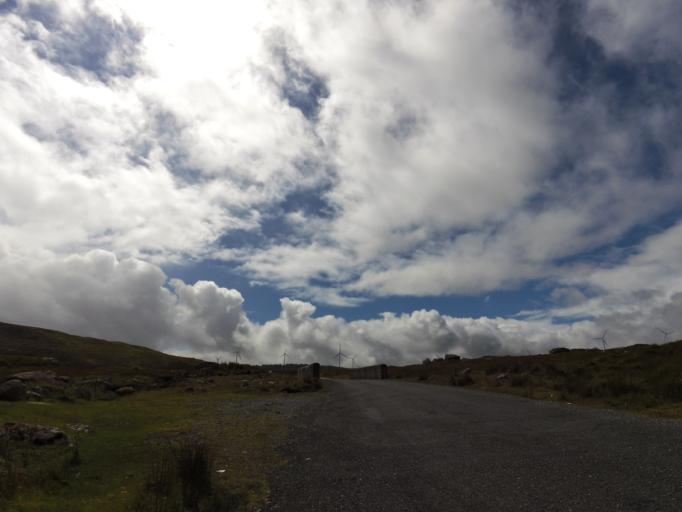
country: IE
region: Connaught
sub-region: County Galway
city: Oughterard
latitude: 53.3891
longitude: -9.3519
